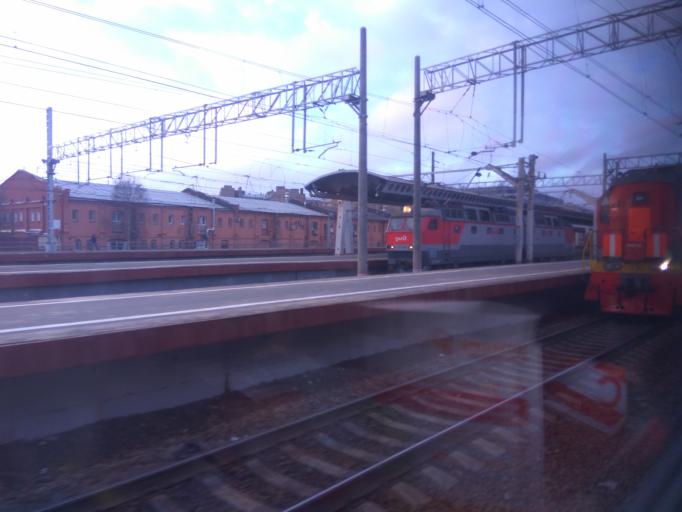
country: RU
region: St.-Petersburg
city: Centralniy
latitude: 59.9242
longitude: 30.3644
